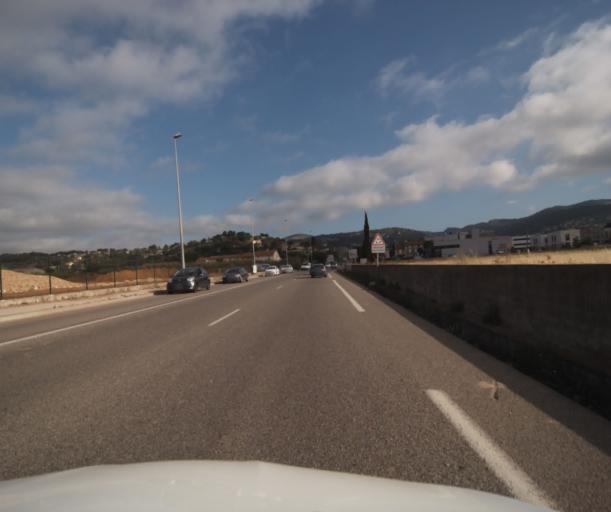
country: FR
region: Provence-Alpes-Cote d'Azur
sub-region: Departement du Var
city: Ollioules
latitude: 43.1245
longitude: 5.8463
